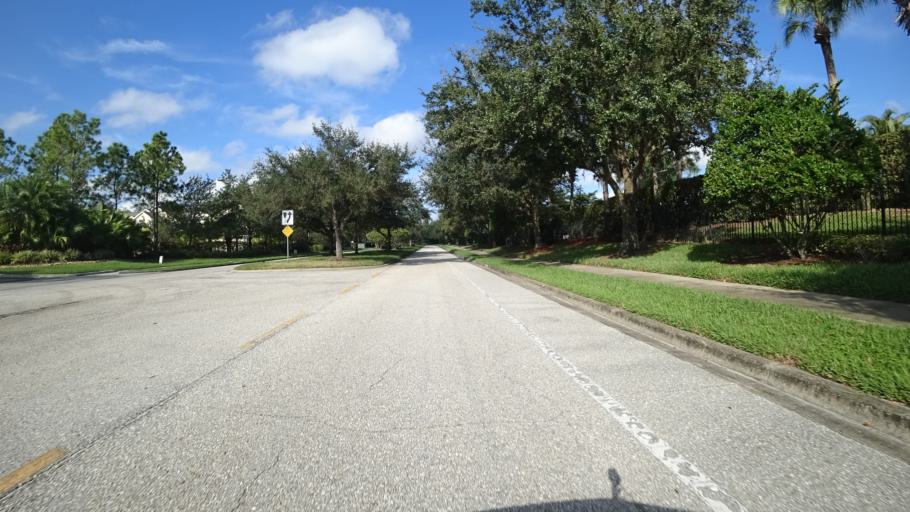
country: US
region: Florida
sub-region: Sarasota County
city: The Meadows
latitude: 27.3990
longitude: -82.4598
